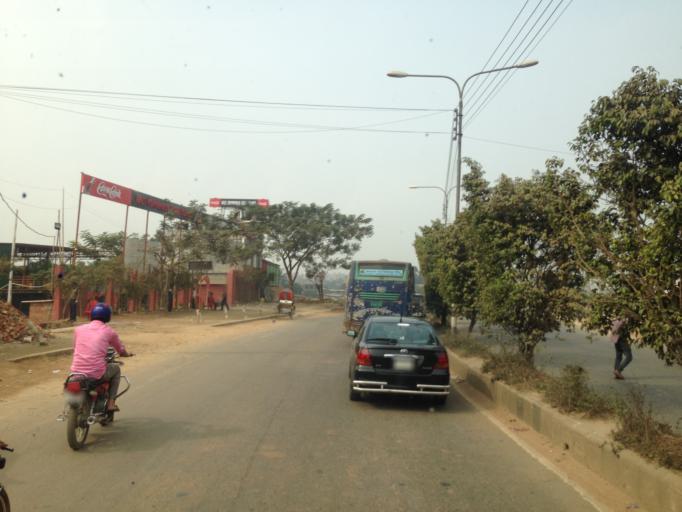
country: BD
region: Dhaka
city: Tungi
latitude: 23.8206
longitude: 90.3849
